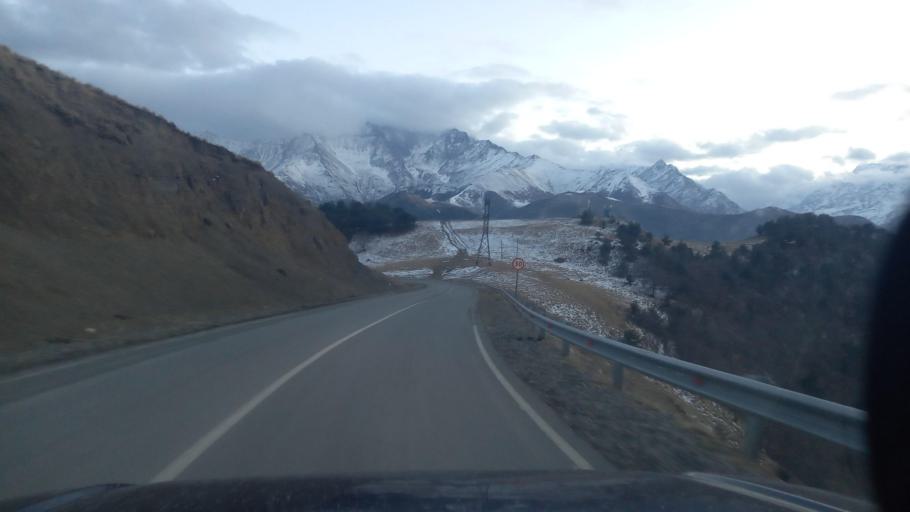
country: RU
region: Ingushetiya
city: Dzhayrakh
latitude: 42.8196
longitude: 44.8388
